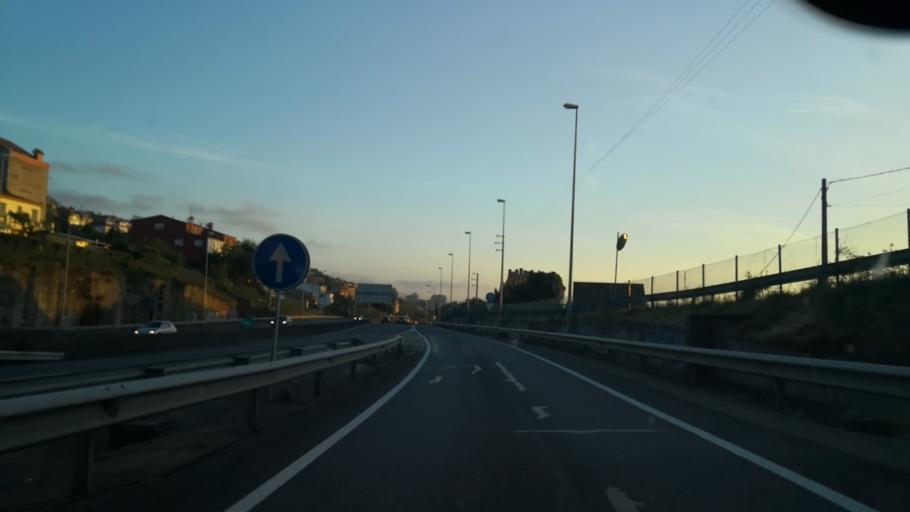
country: ES
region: Galicia
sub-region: Provincia de Pontevedra
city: Vigo
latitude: 42.2575
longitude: -8.6775
